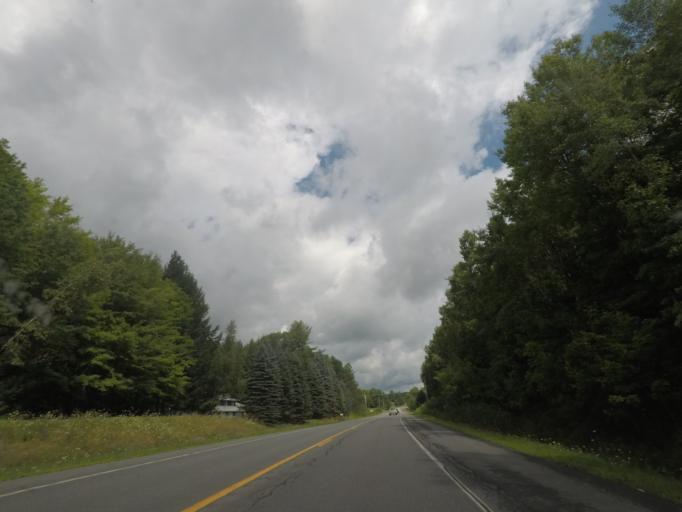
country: US
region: Massachusetts
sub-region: Berkshire County
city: Lanesborough
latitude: 42.5540
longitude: -73.3746
